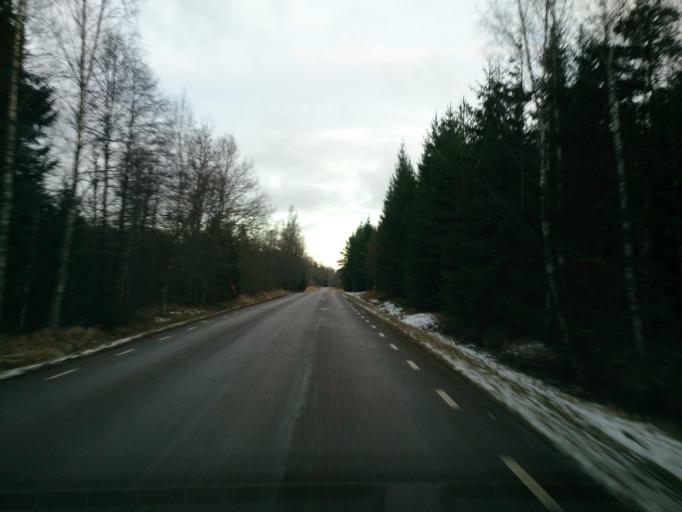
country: SE
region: OEstergoetland
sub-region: Atvidabergs Kommun
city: Atvidaberg
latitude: 58.2586
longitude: 16.0244
